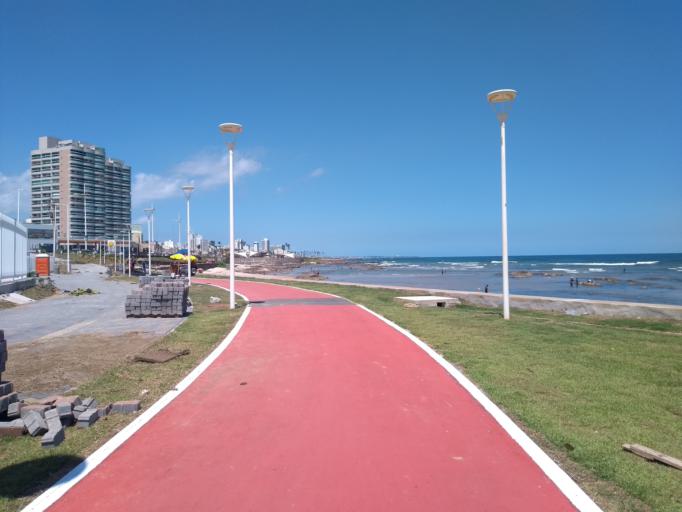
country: BR
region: Bahia
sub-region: Salvador
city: Salvador
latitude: -13.0062
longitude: -38.4546
